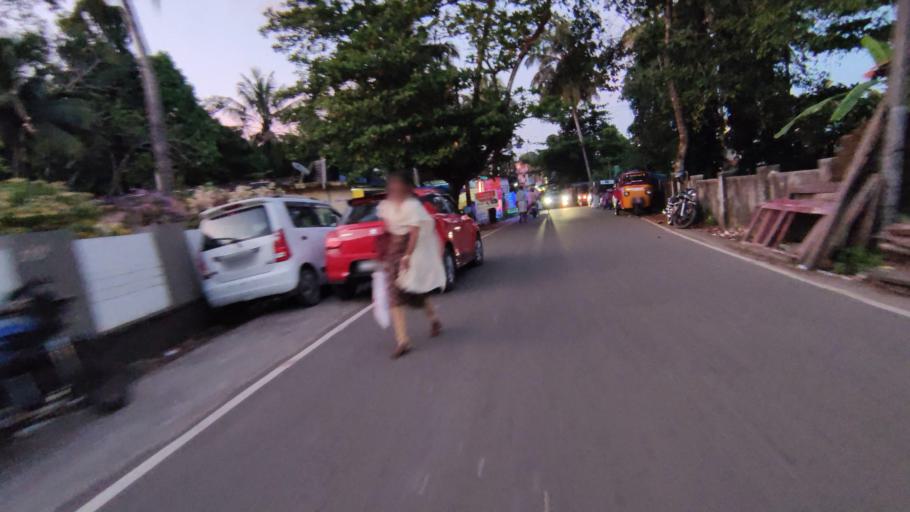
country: IN
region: Kerala
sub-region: Kottayam
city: Kottayam
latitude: 9.5903
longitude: 76.4370
